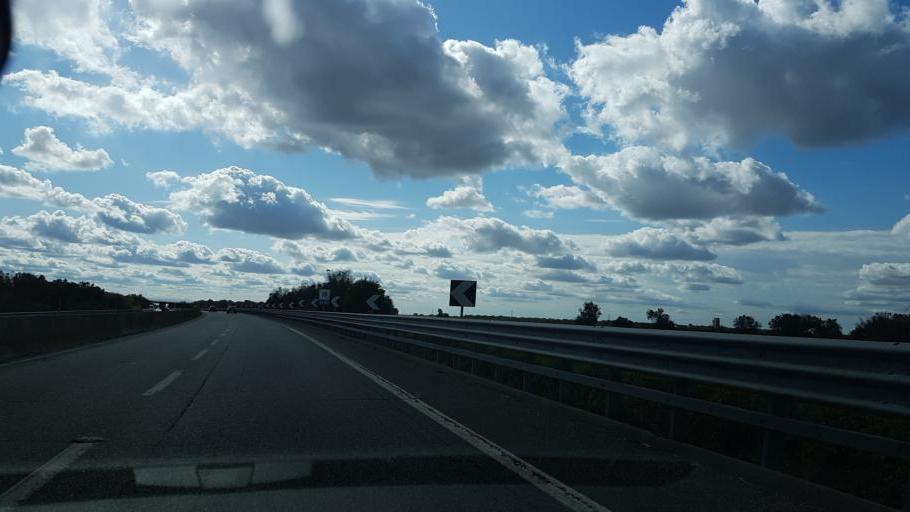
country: IT
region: Apulia
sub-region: Provincia di Brindisi
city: San Pietro Vernotico
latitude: 40.5419
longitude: 18.0017
